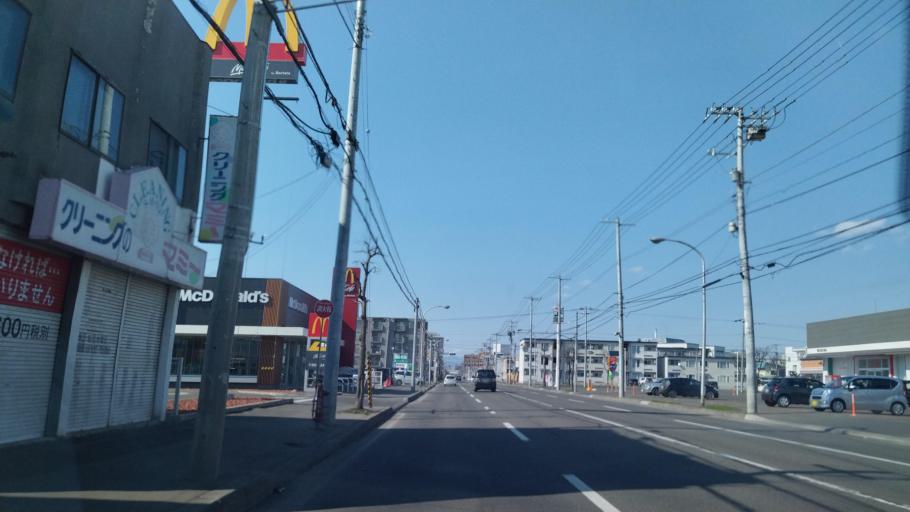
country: JP
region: Hokkaido
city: Obihiro
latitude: 42.9107
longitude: 143.1989
